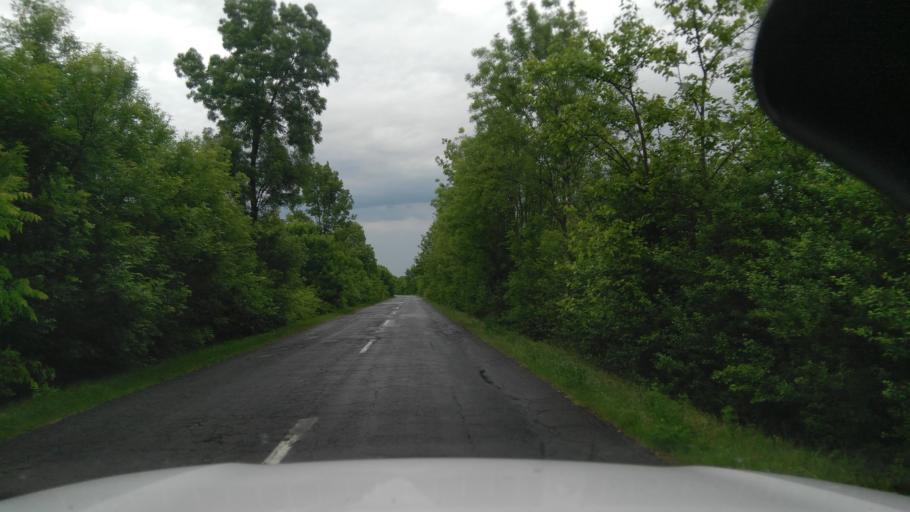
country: HU
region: Bekes
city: Bekescsaba
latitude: 46.6945
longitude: 21.1700
